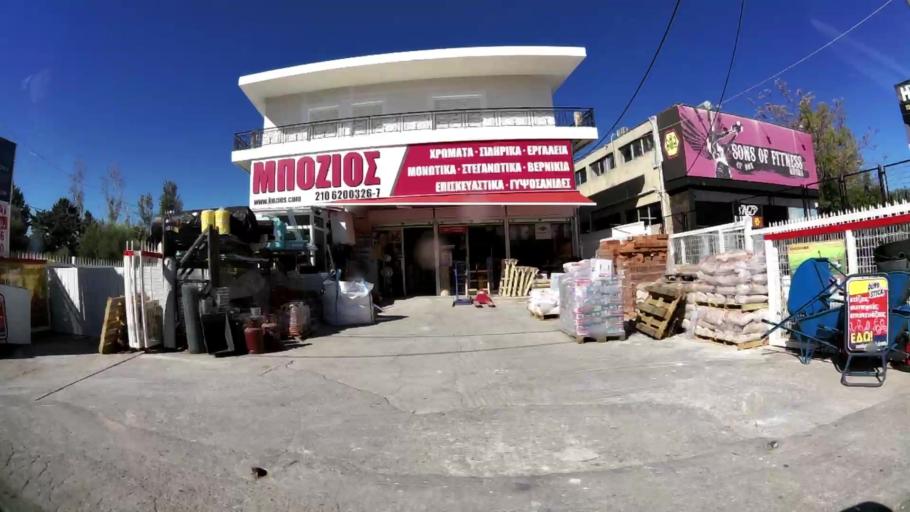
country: GR
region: Attica
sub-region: Nomarchia Athinas
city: Kifisia
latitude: 38.0836
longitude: 23.7976
